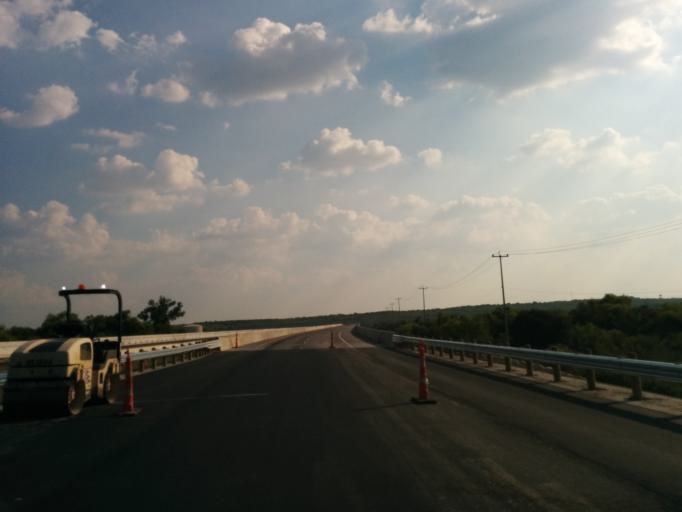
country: US
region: Texas
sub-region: Bexar County
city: Converse
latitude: 29.4864
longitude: -98.2926
